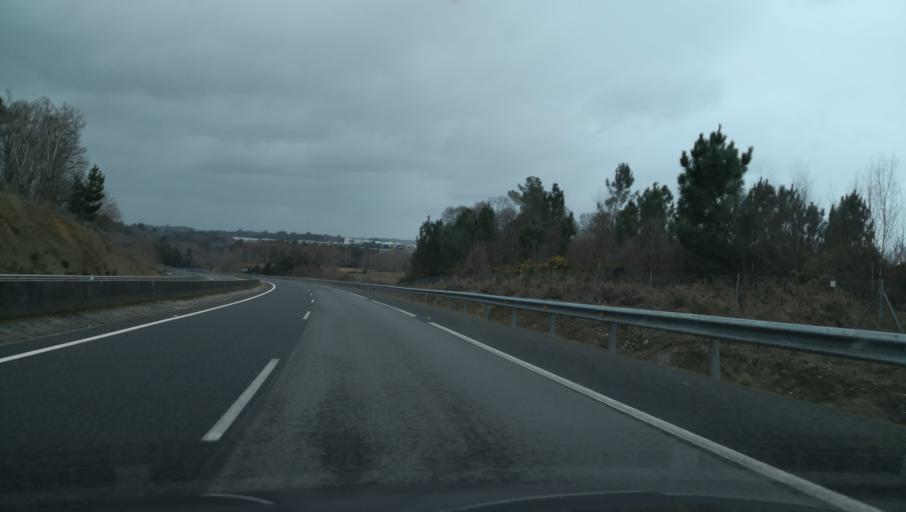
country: ES
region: Galicia
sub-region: Provincia de Pontevedra
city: Lalin
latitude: 42.6584
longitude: -8.1410
